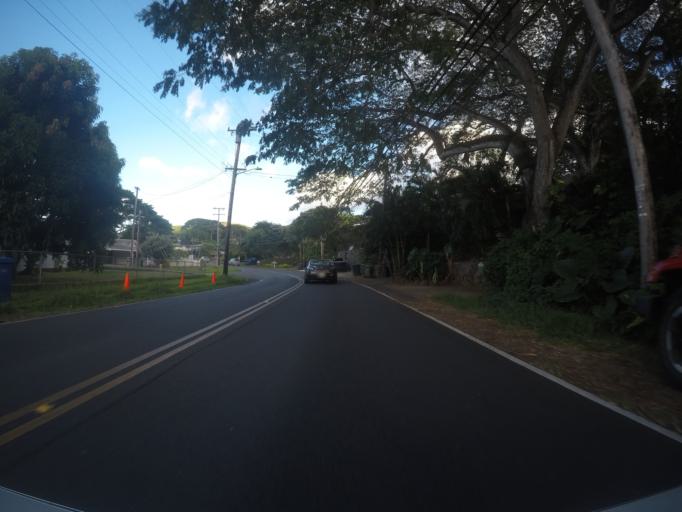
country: US
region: Hawaii
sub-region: Honolulu County
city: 'Ahuimanu
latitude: 21.4520
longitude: -157.8241
